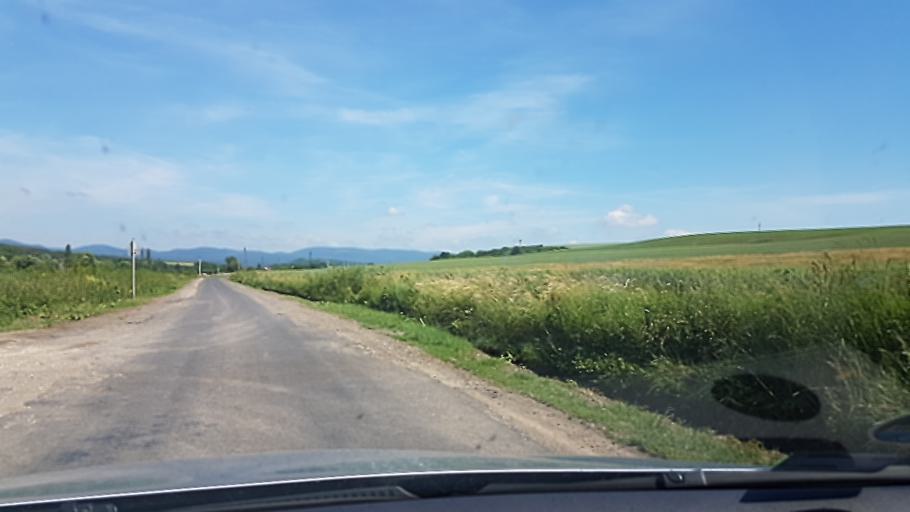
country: HU
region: Borsod-Abauj-Zemplen
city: Saly
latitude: 47.9455
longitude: 20.7038
